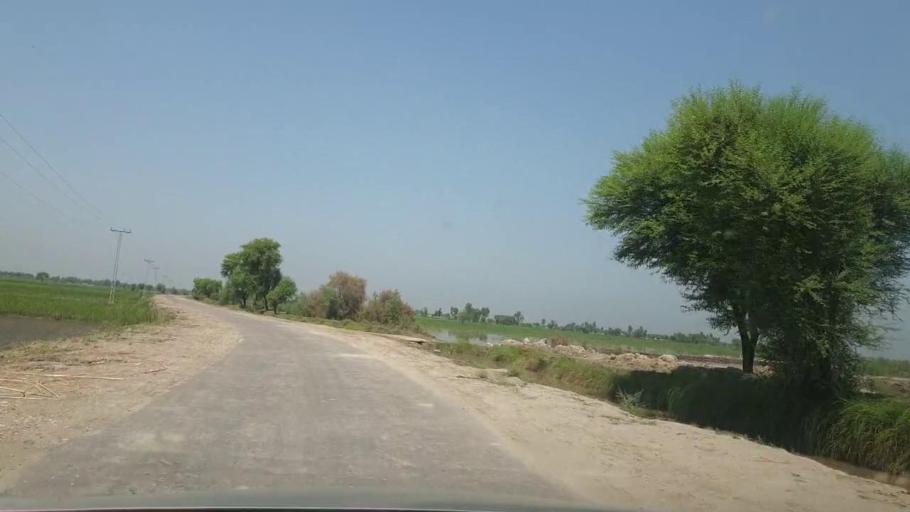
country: PK
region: Sindh
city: Warah
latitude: 27.4719
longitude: 67.7631
